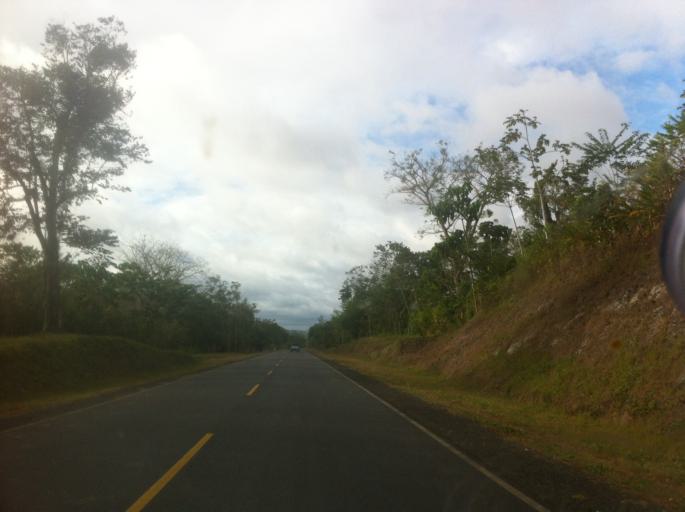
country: NI
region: Rio San Juan
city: San Carlos
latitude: 11.2022
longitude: -84.6815
